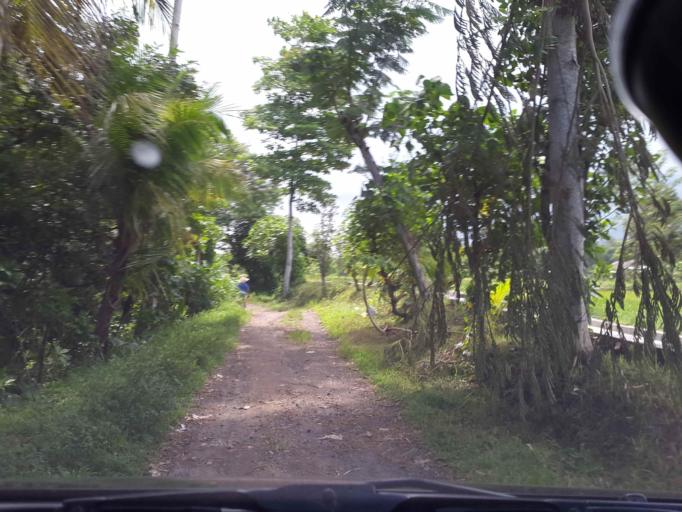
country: ID
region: West Nusa Tenggara
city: Batukuta
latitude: -8.6039
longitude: 116.1918
